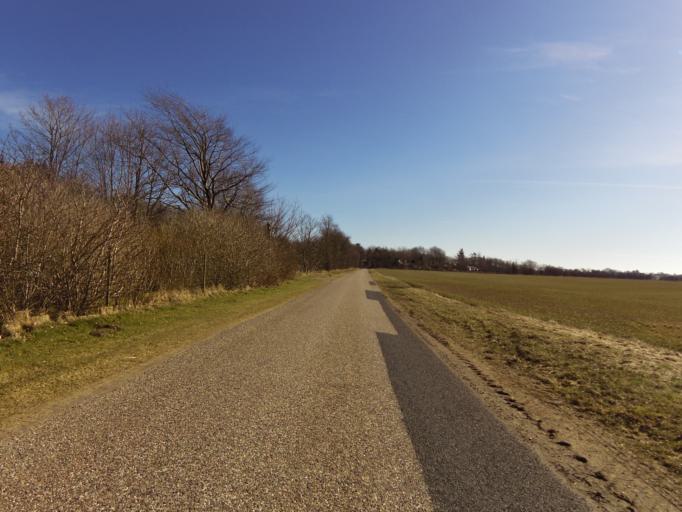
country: DK
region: South Denmark
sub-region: Tonder Kommune
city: Toftlund
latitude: 55.2282
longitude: 9.1399
